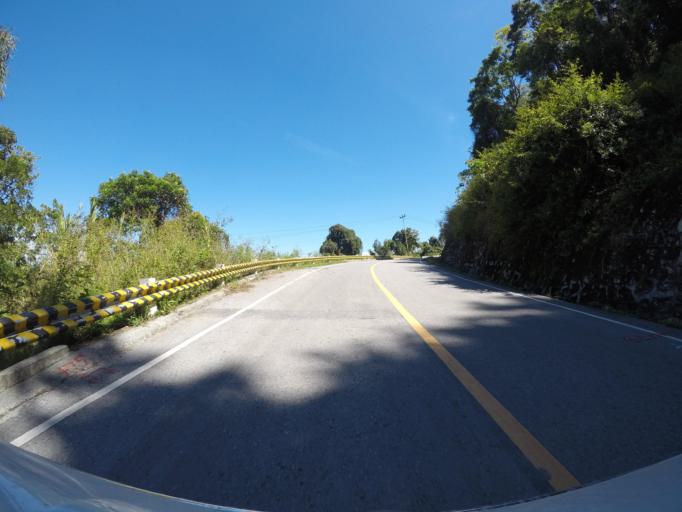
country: TL
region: Manufahi
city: Same
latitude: -8.9024
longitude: 125.9773
